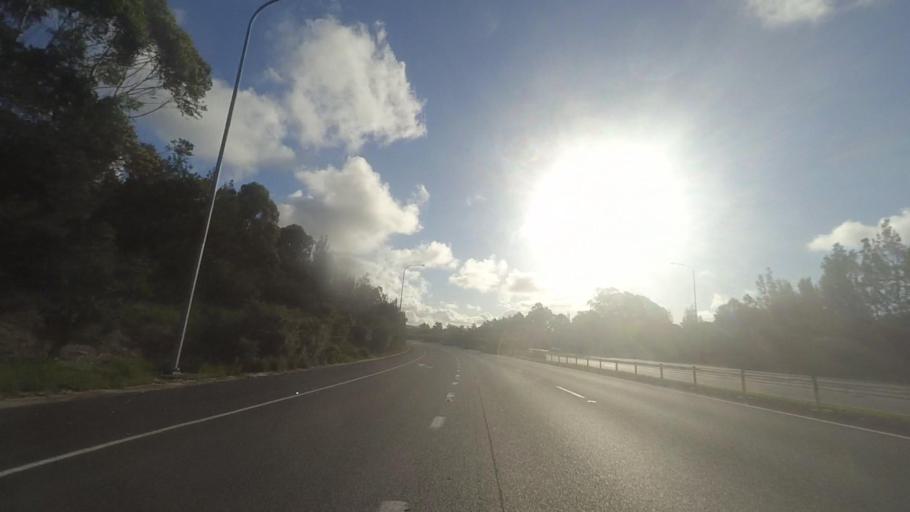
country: AU
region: New South Wales
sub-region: Great Lakes
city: Nabiac
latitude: -32.0961
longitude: 152.3788
